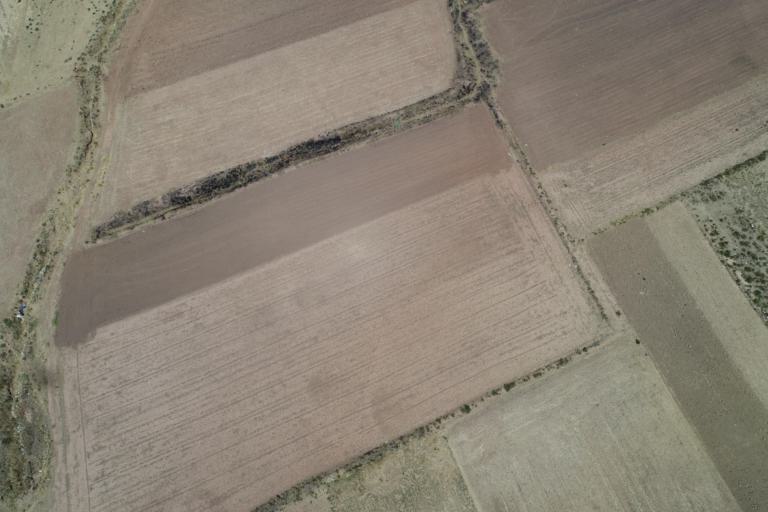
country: BO
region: La Paz
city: Achacachi
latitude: -15.9140
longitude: -68.8868
